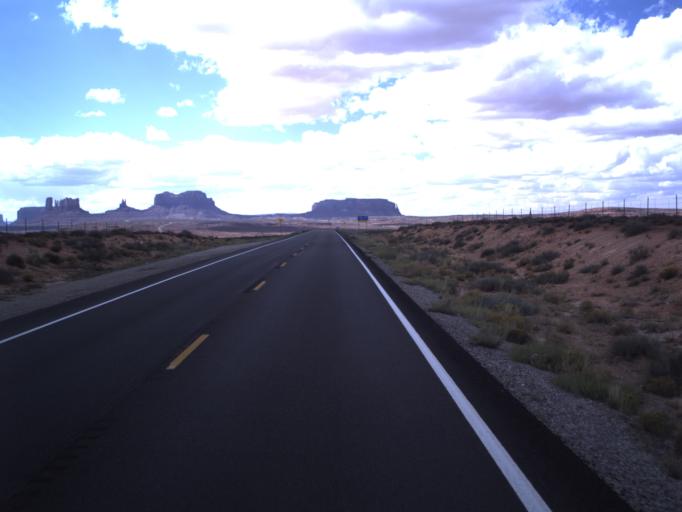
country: US
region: Arizona
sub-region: Navajo County
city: Kayenta
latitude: 37.1072
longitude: -109.9802
